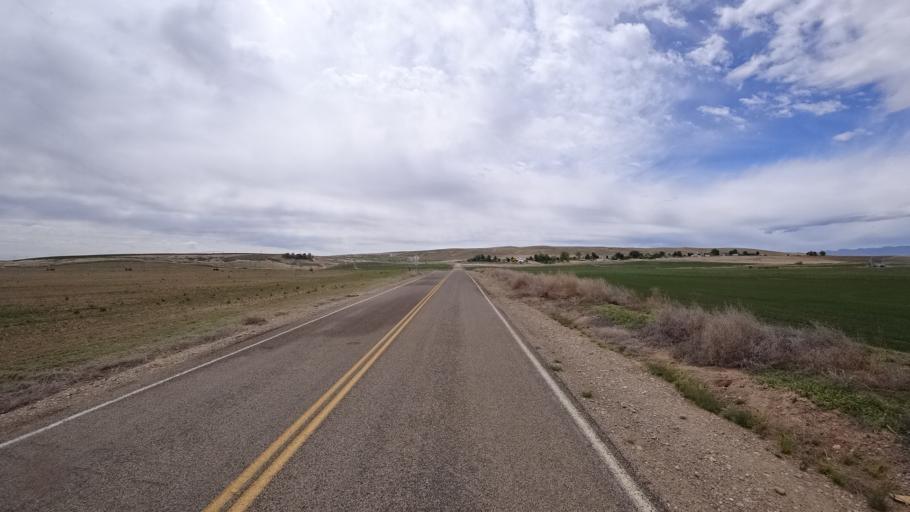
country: US
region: Idaho
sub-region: Ada County
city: Kuna
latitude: 43.4675
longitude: -116.4432
